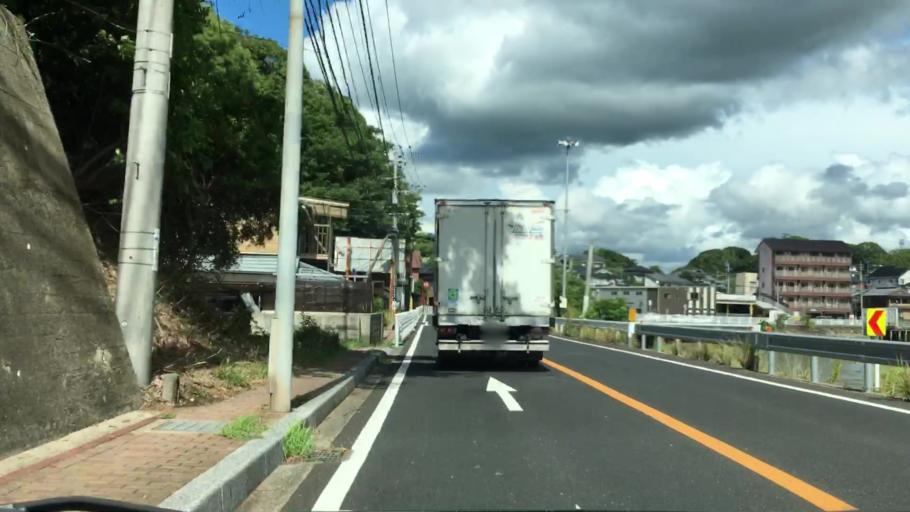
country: JP
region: Nagasaki
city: Sasebo
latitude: 33.1389
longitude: 129.7908
